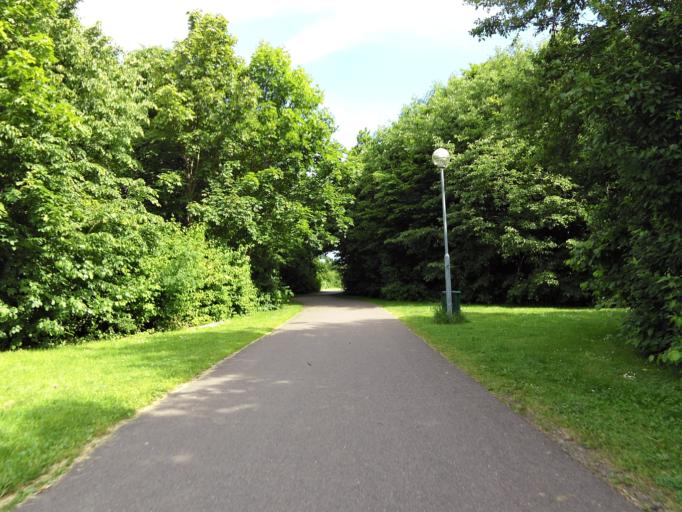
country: SE
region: Skane
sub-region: Lomma Kommun
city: Lomma
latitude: 55.6783
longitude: 13.0868
